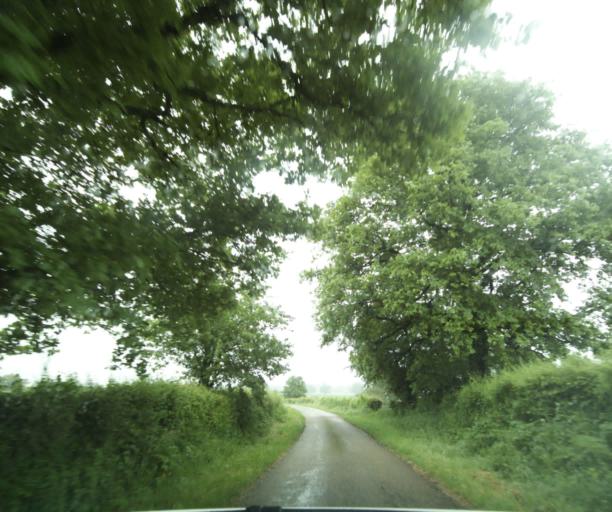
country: FR
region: Bourgogne
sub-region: Departement de Saone-et-Loire
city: Charolles
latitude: 46.4606
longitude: 4.2307
